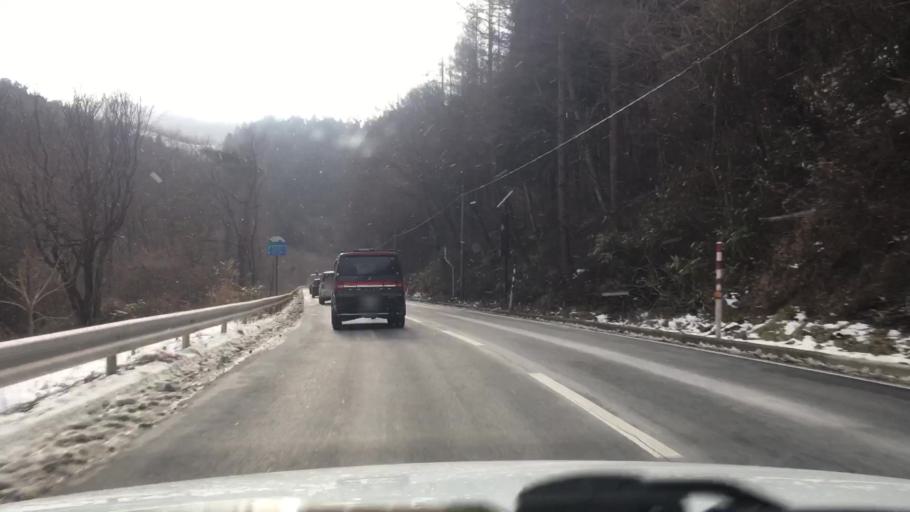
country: JP
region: Iwate
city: Morioka-shi
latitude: 39.6683
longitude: 141.3232
